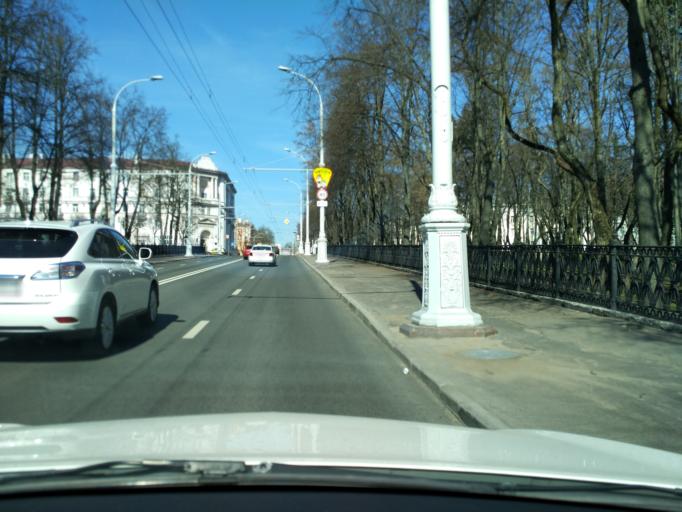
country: BY
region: Minsk
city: Minsk
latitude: 53.9094
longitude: 27.5632
